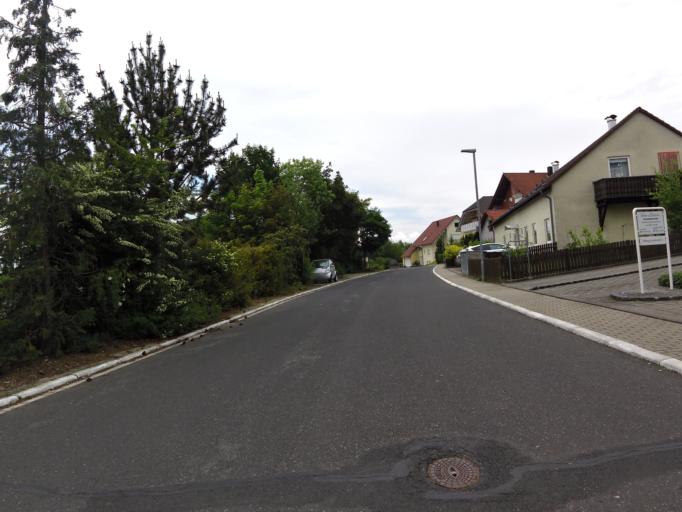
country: DE
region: Bavaria
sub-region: Regierungsbezirk Unterfranken
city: Kleinrinderfeld
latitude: 49.7052
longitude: 9.7903
